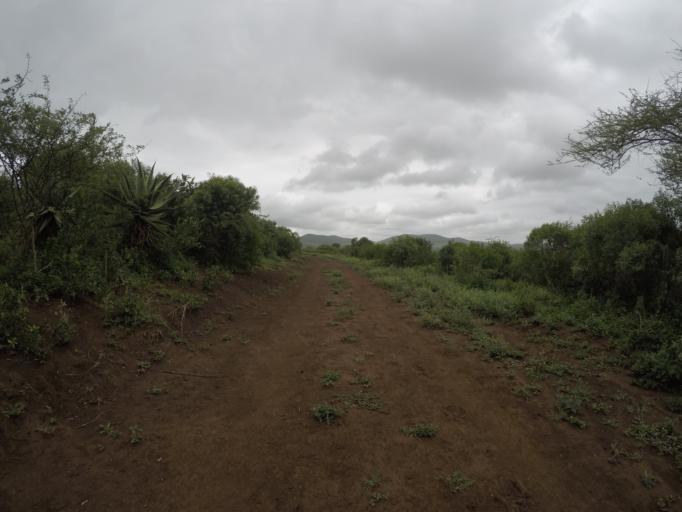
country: ZA
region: KwaZulu-Natal
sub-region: uThungulu District Municipality
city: Empangeni
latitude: -28.6013
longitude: 31.8516
